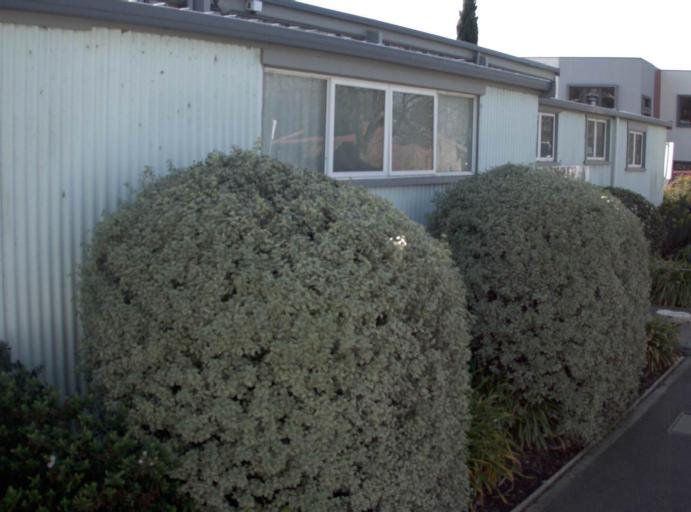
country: AU
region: Tasmania
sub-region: Launceston
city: Launceston
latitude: -41.4351
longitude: 147.1303
